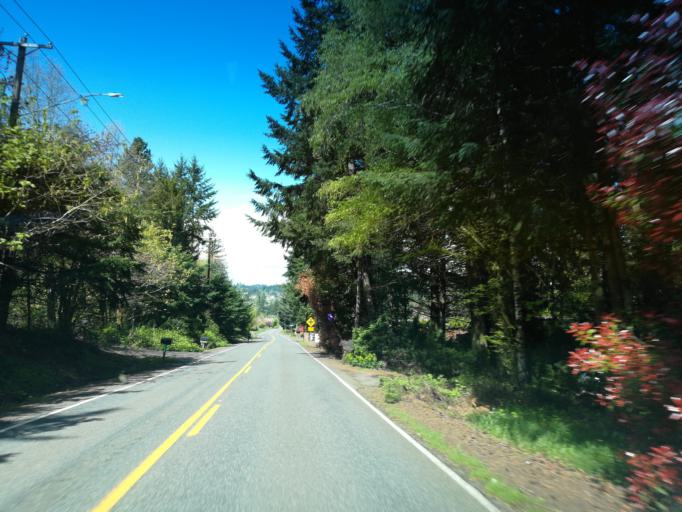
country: US
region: Oregon
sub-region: Clackamas County
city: Damascus
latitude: 45.4288
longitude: -122.4344
